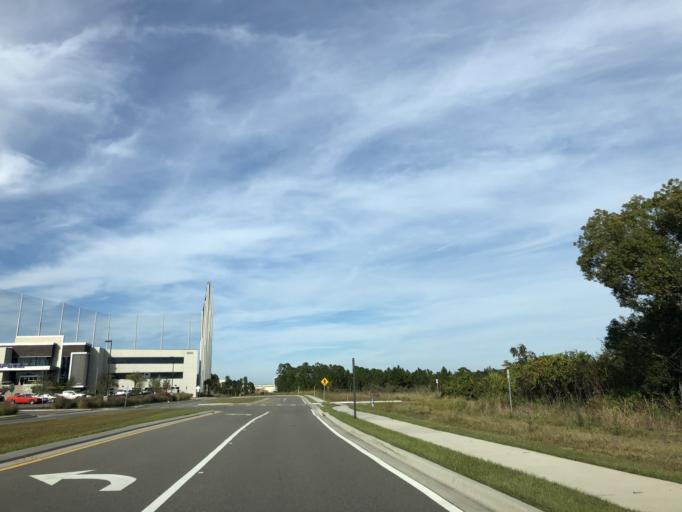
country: US
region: Florida
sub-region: Orange County
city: Tangelo Park
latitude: 28.4343
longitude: -81.4632
